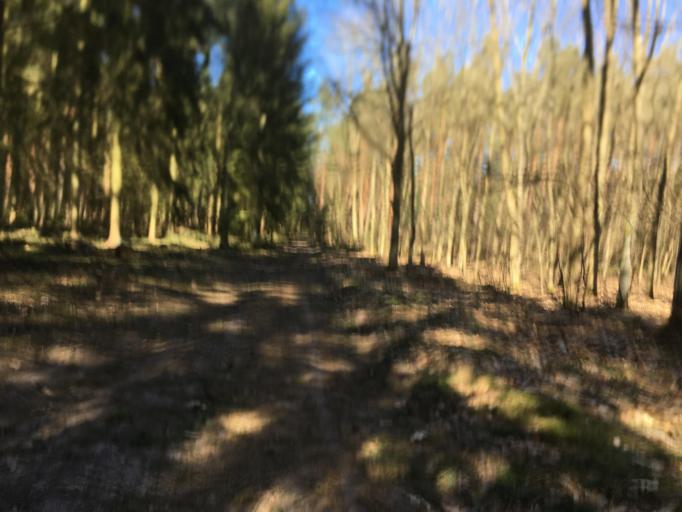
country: DE
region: Brandenburg
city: Wandlitz
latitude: 52.7370
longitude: 13.5138
